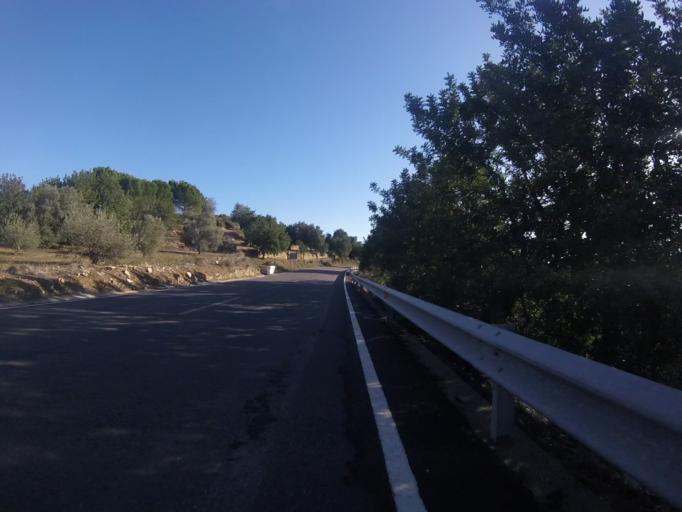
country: ES
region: Valencia
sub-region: Provincia de Castello
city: Cuevas de Vinroma
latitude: 40.3124
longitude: 0.1476
